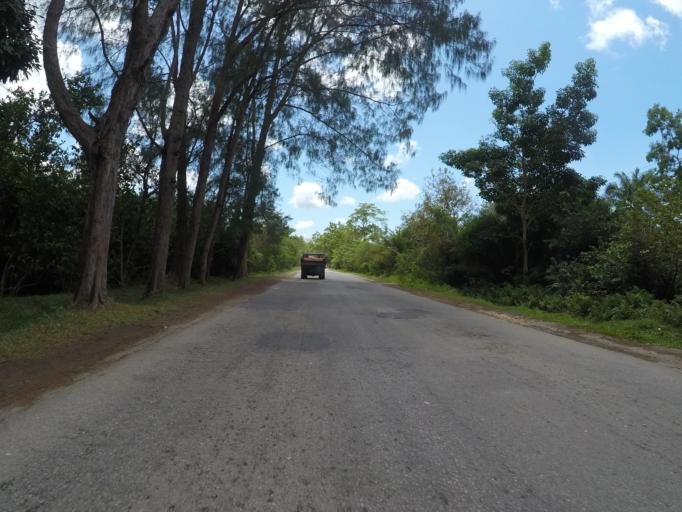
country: TZ
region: Zanzibar Central/South
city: Mahonda
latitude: -6.2759
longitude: 39.4164
